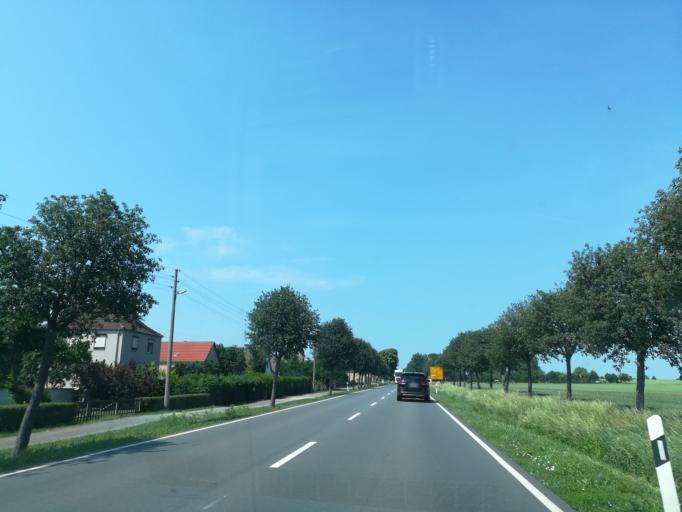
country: DE
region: Saxony-Anhalt
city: Aschersleben
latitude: 51.8217
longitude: 11.4568
